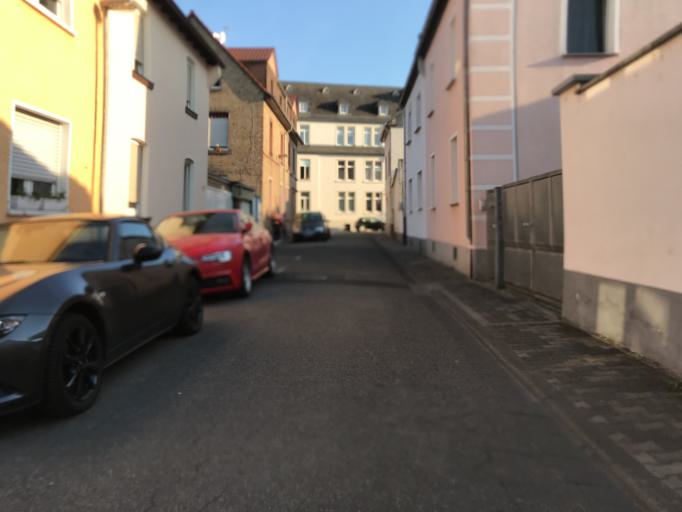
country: DE
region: Rheinland-Pfalz
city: Budenheim
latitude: 50.0210
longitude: 8.2256
